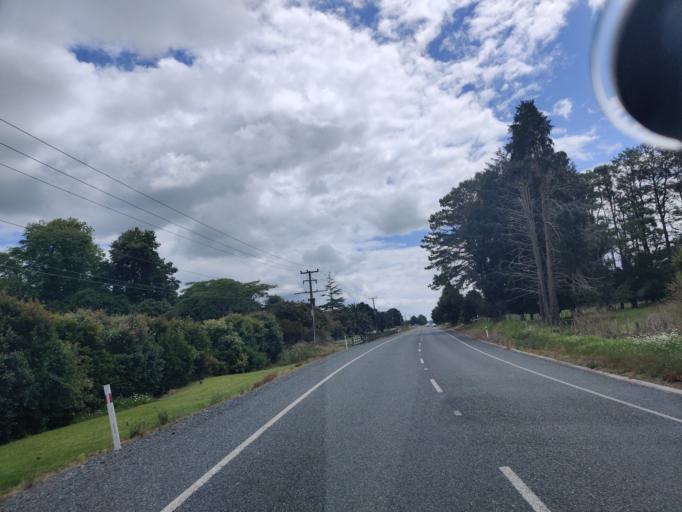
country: NZ
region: Northland
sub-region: Far North District
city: Kerikeri
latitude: -35.2923
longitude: 173.9897
